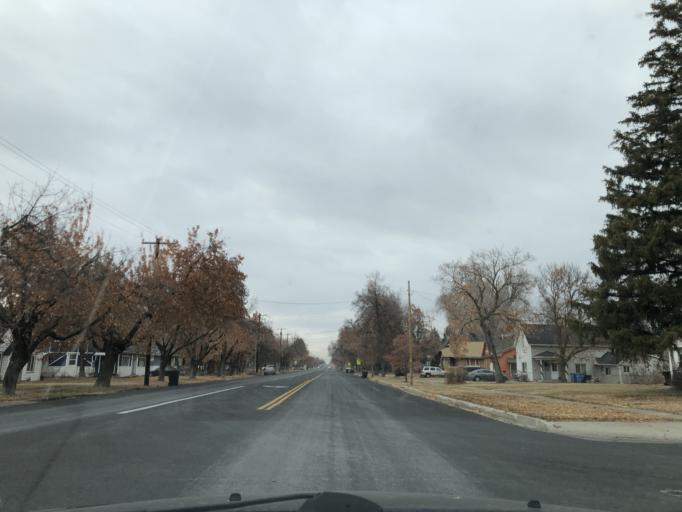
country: US
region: Utah
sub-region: Cache County
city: Logan
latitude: 41.7222
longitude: -111.8379
